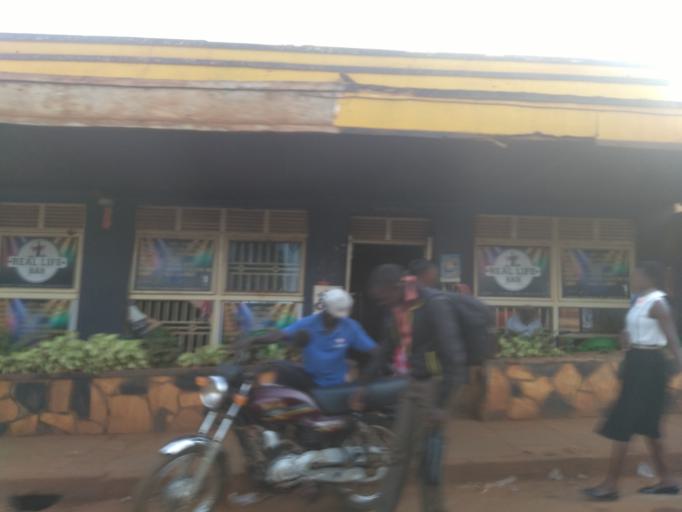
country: UG
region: Eastern Region
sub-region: Jinja District
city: Jinja
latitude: 0.4334
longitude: 33.2126
